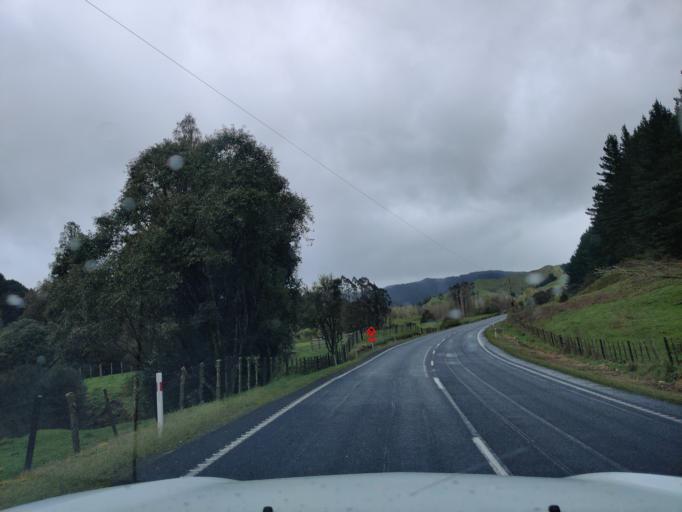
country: NZ
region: Waikato
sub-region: Otorohanga District
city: Otorohanga
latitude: -38.6648
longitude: 175.2065
